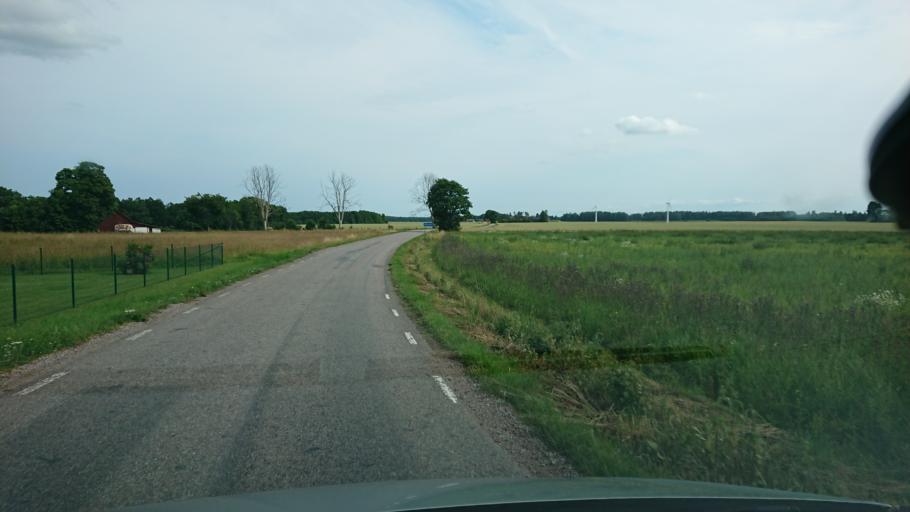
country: SE
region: Uppsala
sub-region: Osthammars Kommun
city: Bjorklinge
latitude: 59.9854
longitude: 17.5564
